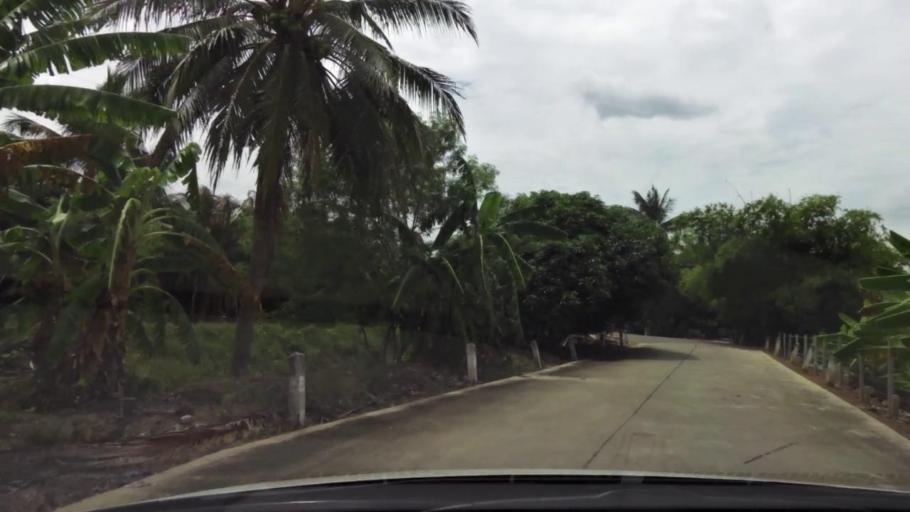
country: TH
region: Ratchaburi
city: Damnoen Saduak
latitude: 13.5515
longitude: 99.9956
